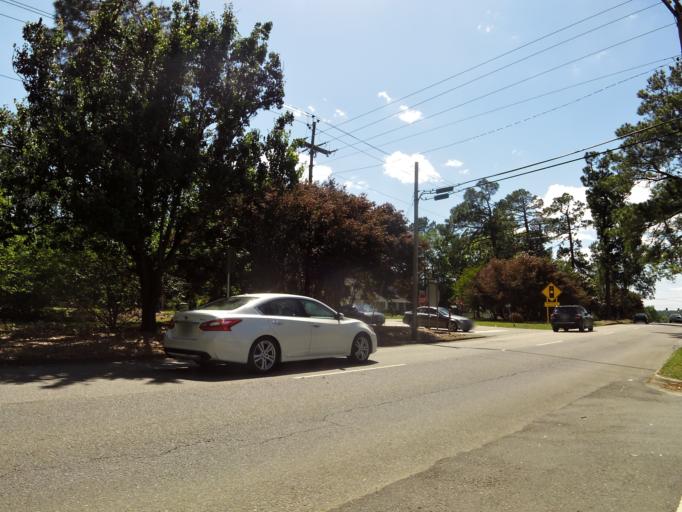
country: US
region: South Carolina
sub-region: Aiken County
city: Aiken
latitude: 33.5641
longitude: -81.7295
